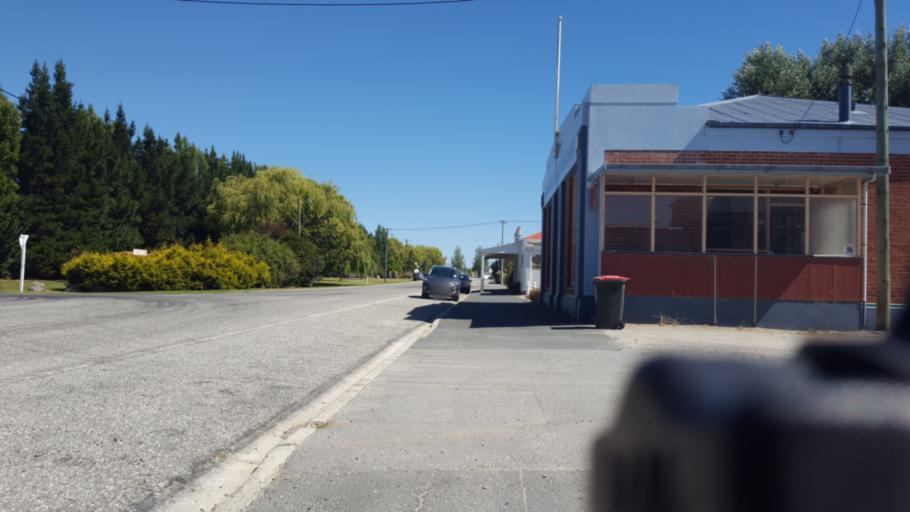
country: NZ
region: Otago
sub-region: Dunedin City
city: Dunedin
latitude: -45.1286
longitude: 170.0980
